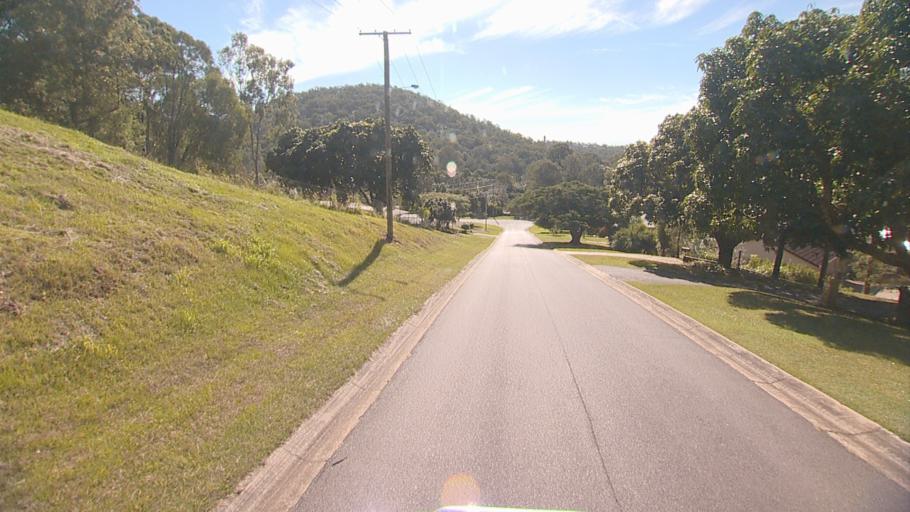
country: AU
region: Queensland
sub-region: Logan
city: Windaroo
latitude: -27.7444
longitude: 153.1832
